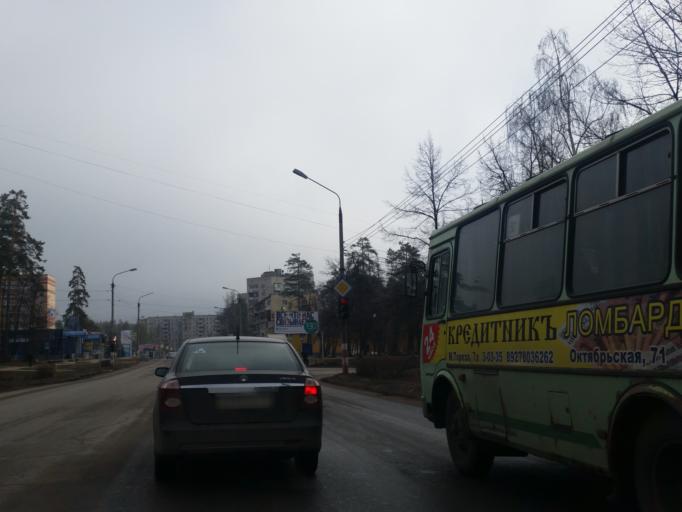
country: RU
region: Ulyanovsk
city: Dimitrovgrad
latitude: 54.2352
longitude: 49.5597
